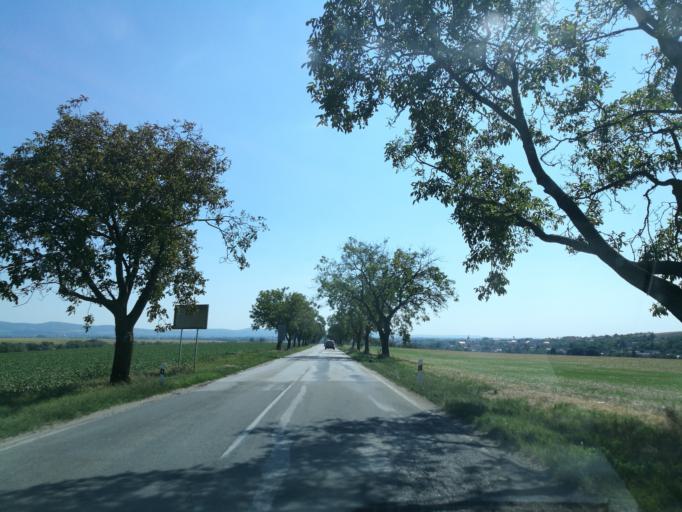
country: SK
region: Trnavsky
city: Vrbove
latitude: 48.6382
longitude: 17.7167
